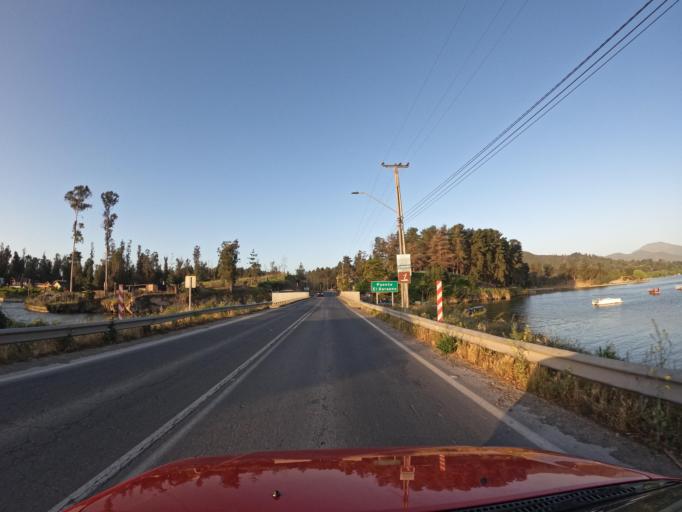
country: CL
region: O'Higgins
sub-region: Provincia de Cachapoal
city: San Vicente
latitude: -34.1465
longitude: -71.3809
